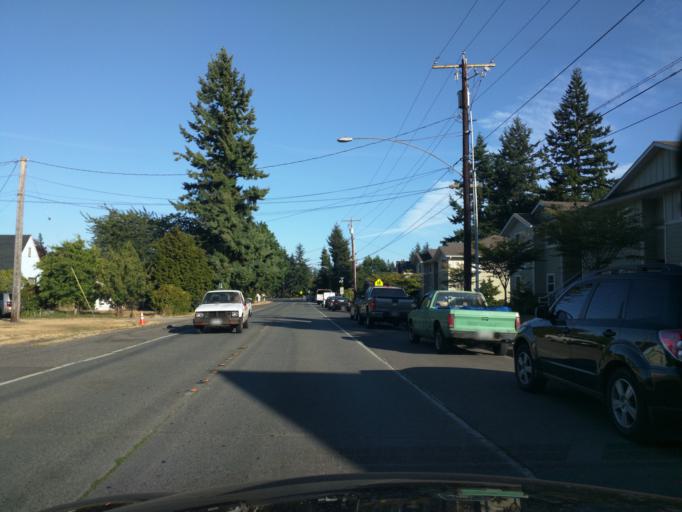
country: US
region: Washington
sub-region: Whatcom County
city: Bellingham
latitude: 48.7786
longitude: -122.5055
